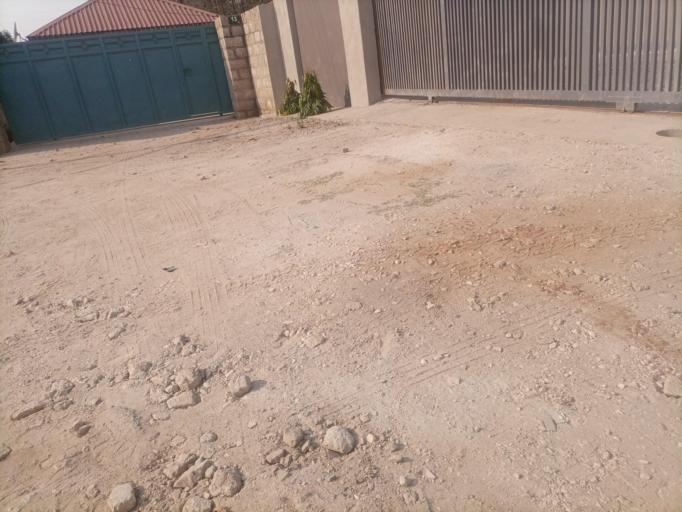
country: ZM
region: Lusaka
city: Lusaka
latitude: -15.4008
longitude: 28.3870
